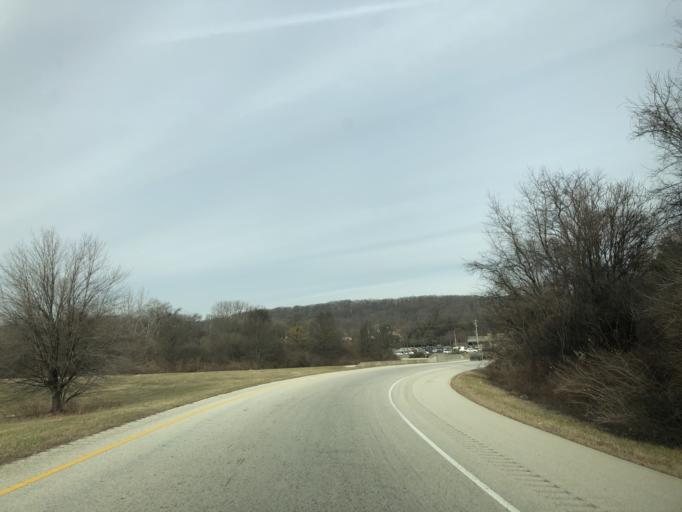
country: US
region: Pennsylvania
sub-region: Chester County
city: Downingtown
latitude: 40.0182
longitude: -75.6692
